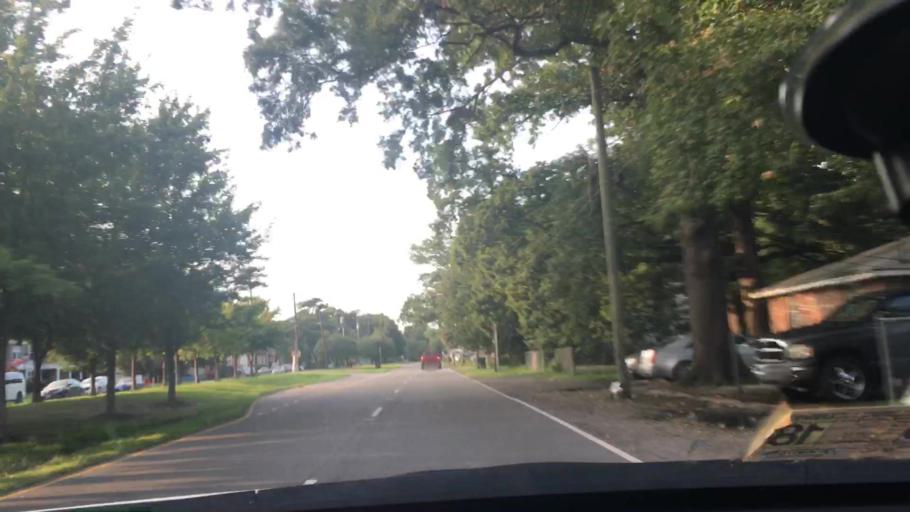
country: US
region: Virginia
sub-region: City of Norfolk
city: Norfolk
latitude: 36.9396
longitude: -76.2452
